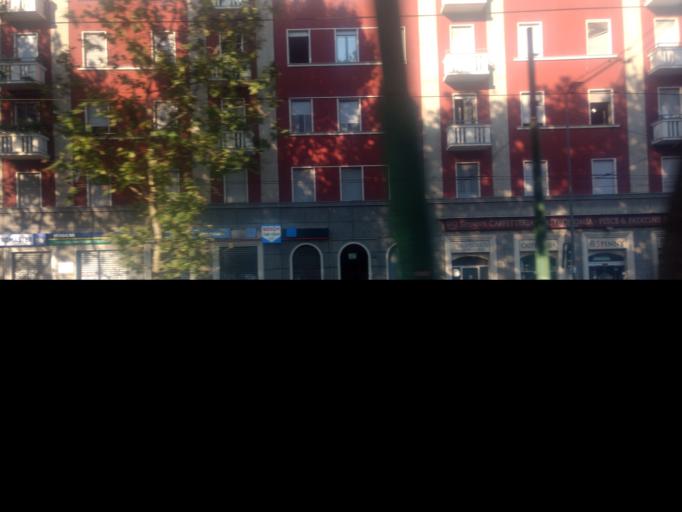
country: IT
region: Lombardy
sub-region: Citta metropolitana di Milano
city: Milano
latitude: 45.4955
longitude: 9.1720
